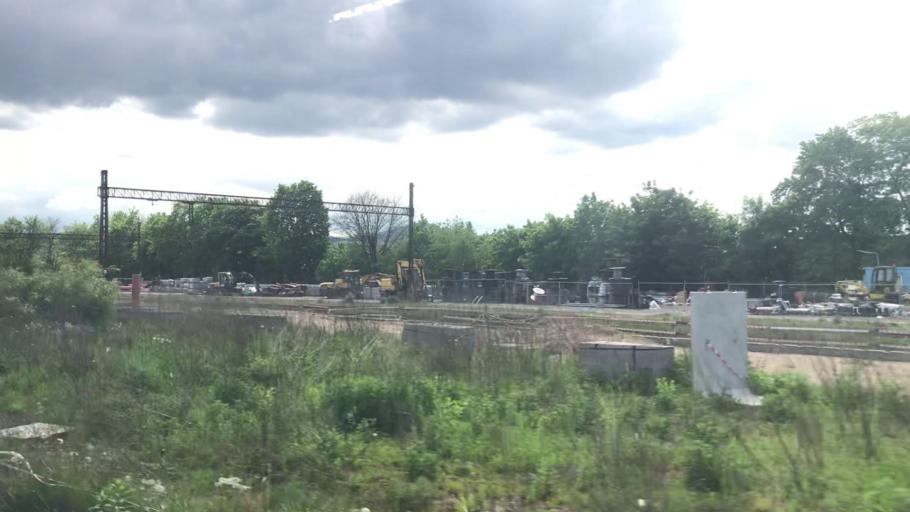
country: PL
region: Lower Silesian Voivodeship
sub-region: Powiat walbrzyski
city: Szczawno-Zdroj
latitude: 50.8169
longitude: 16.3029
